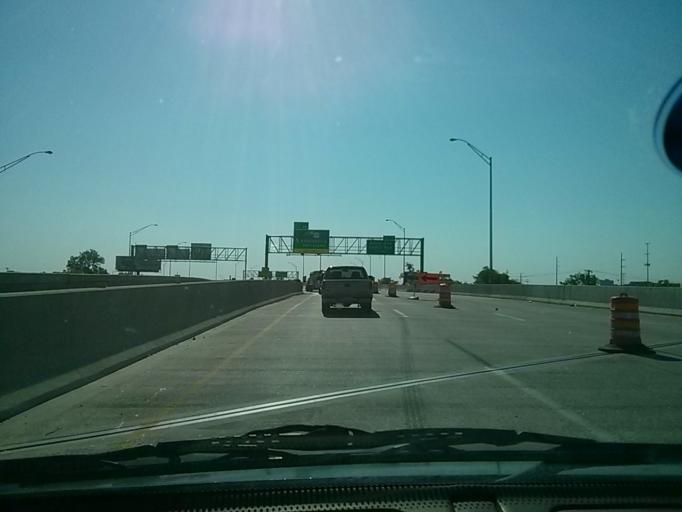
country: US
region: Oklahoma
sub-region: Tulsa County
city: Tulsa
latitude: 36.1608
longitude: -95.9865
